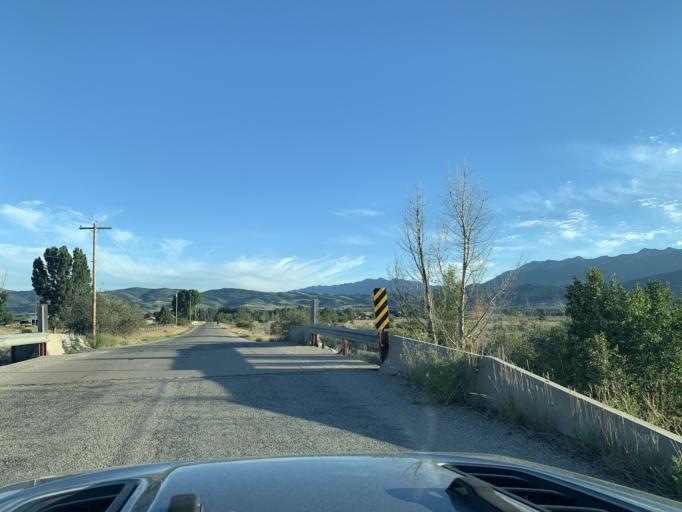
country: US
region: Utah
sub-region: Weber County
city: Wolf Creek
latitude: 41.2909
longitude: -111.7580
